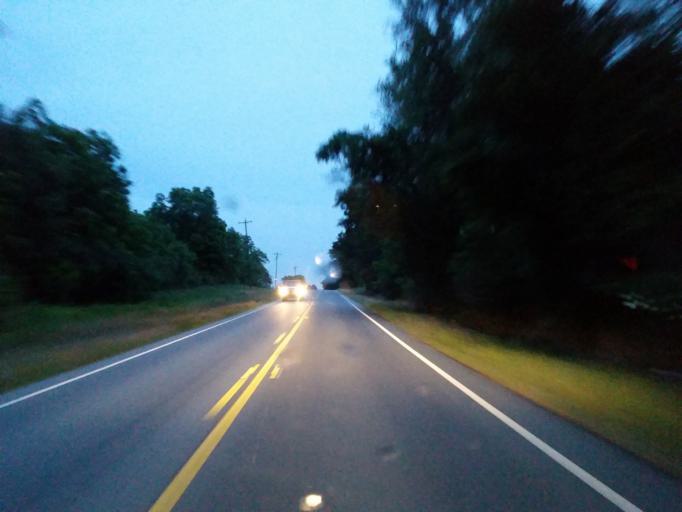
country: US
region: Georgia
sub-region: Turner County
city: Ashburn
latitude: 31.5848
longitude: -83.5744
